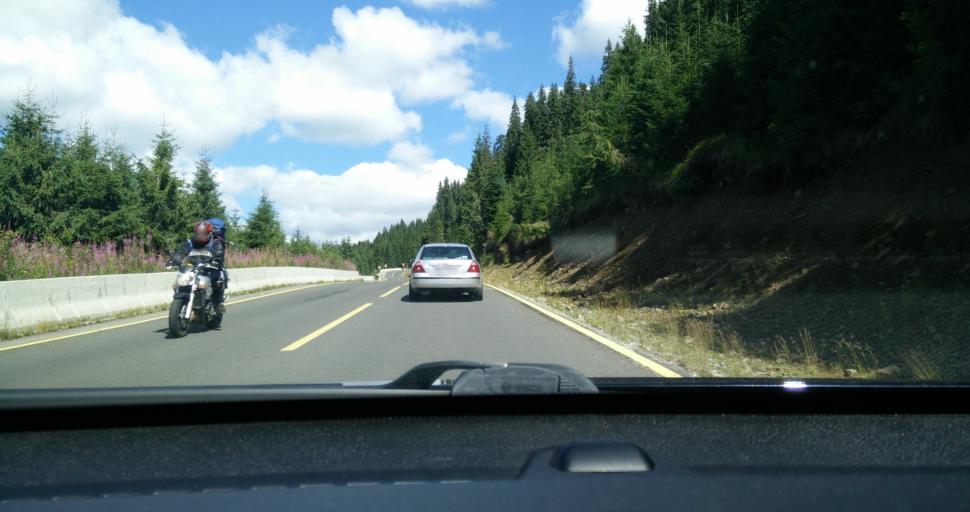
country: RO
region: Hunedoara
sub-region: Oras Petrila
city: Petrila
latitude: 45.4464
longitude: 23.6219
